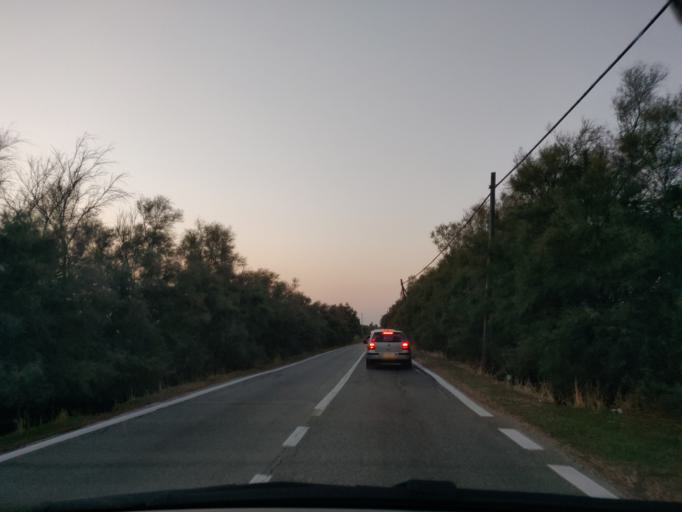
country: IT
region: Latium
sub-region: Citta metropolitana di Roma Capitale
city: Npp 23 (Parco Leonardo)
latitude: 41.8225
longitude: 12.2923
